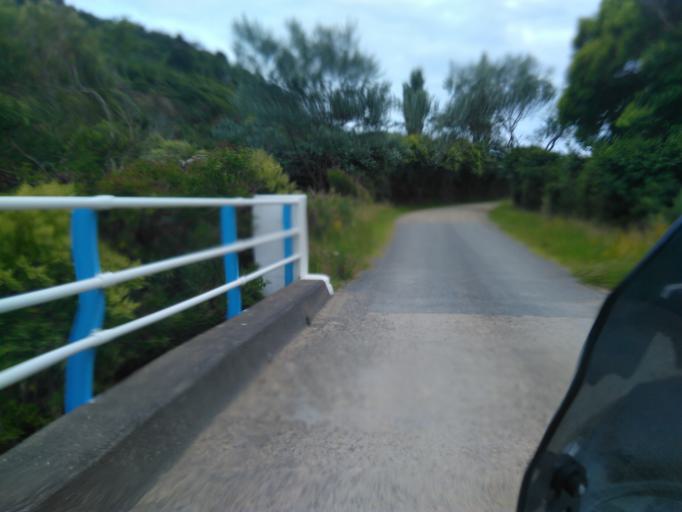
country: NZ
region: Bay of Plenty
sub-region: Opotiki District
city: Opotiki
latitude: -38.0150
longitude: 177.4232
